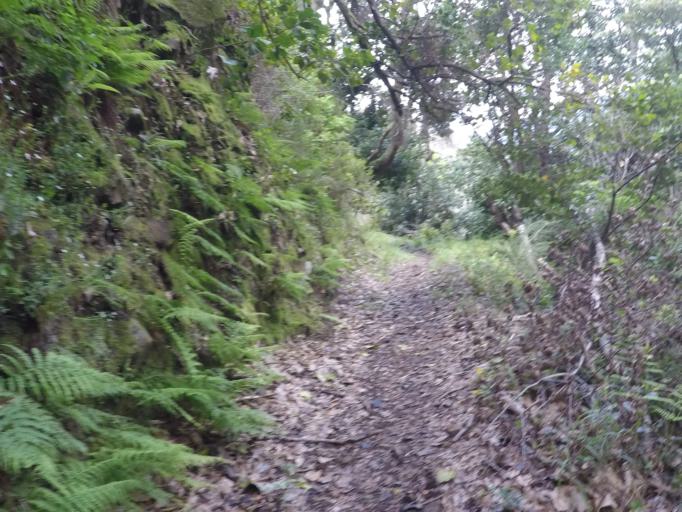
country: PT
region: Madeira
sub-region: Camara de Lobos
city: Curral das Freiras
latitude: 32.7468
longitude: -17.0009
